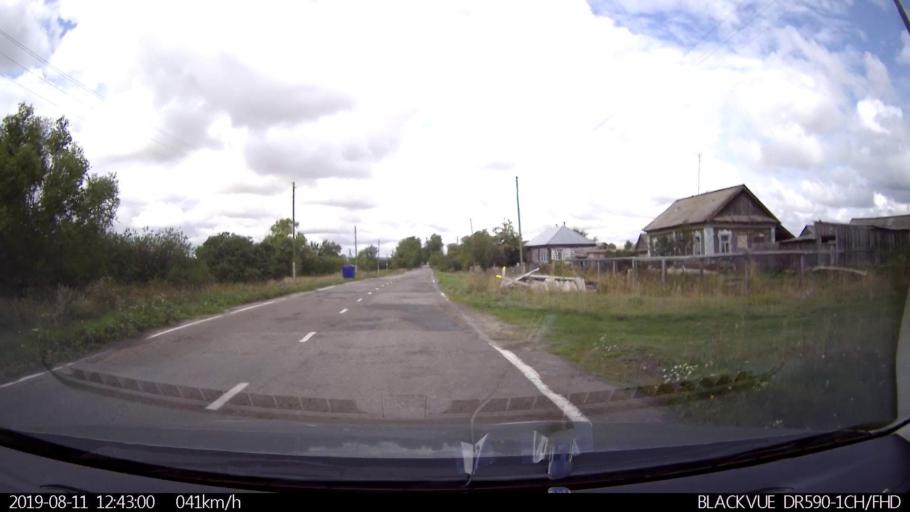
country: RU
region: Ulyanovsk
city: Ignatovka
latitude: 53.8491
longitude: 47.7459
